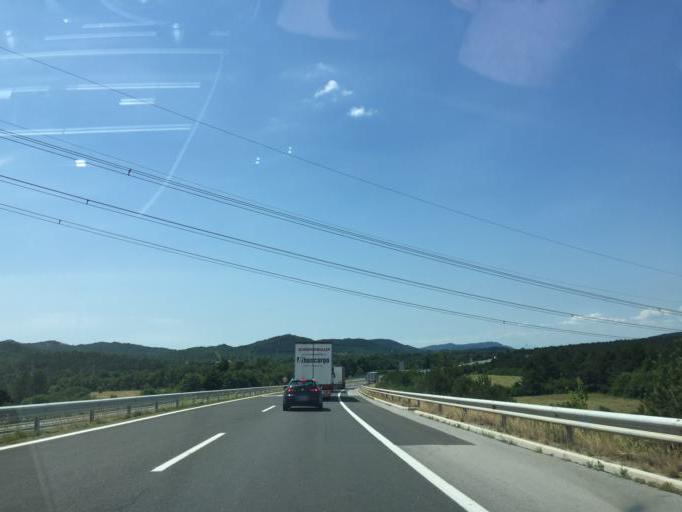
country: SI
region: Divaca
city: Divaca
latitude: 45.6943
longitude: 13.9717
